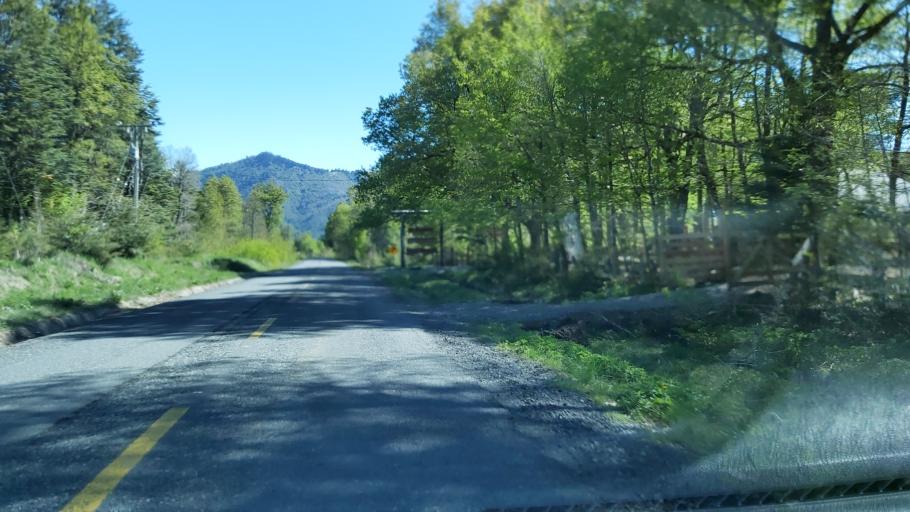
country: CL
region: Araucania
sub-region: Provincia de Cautin
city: Vilcun
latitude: -38.4715
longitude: -71.5257
